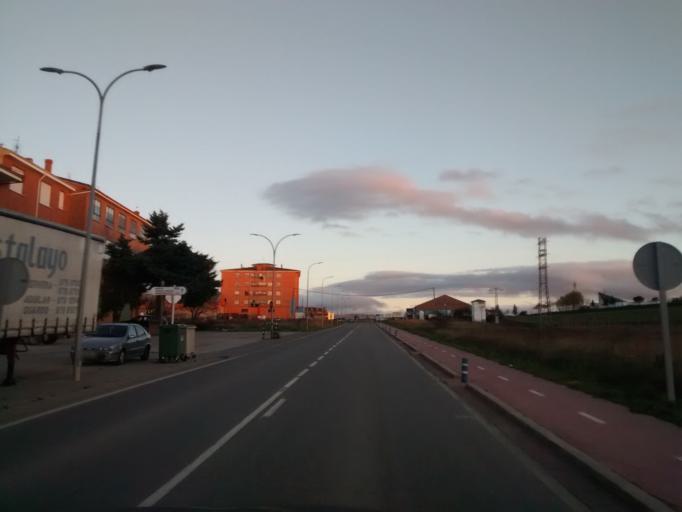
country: ES
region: Castille and Leon
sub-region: Provincia de Palencia
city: Aguilar de Campoo
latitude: 42.7928
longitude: -4.2537
